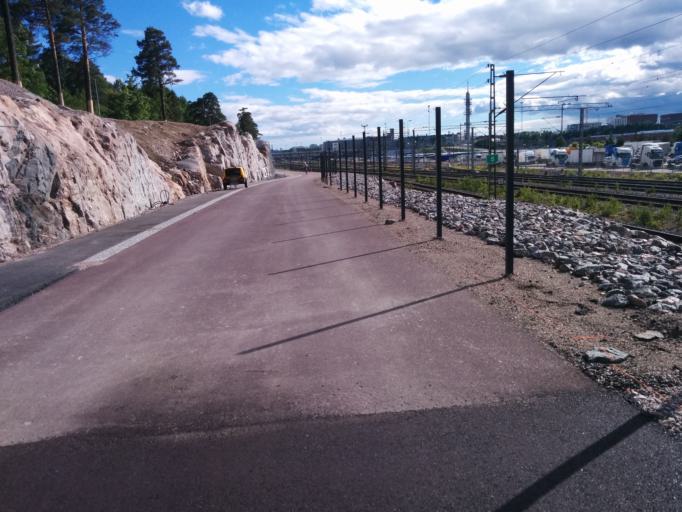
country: FI
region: Uusimaa
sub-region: Helsinki
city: Helsinki
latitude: 60.2143
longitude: 24.9377
